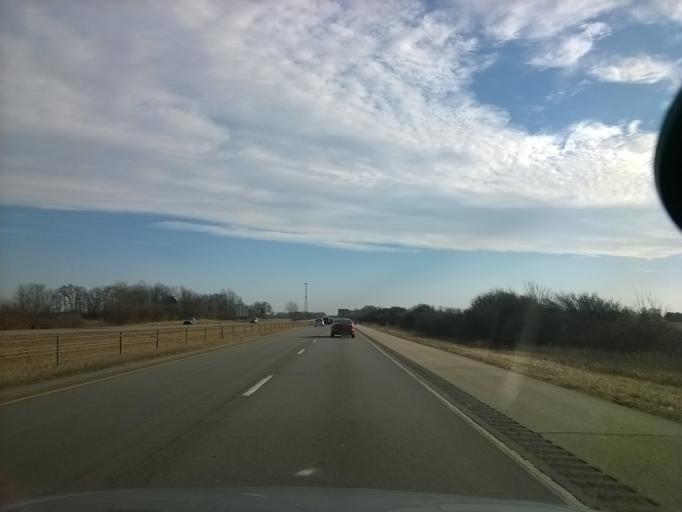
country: US
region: Indiana
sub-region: Johnson County
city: Franklin
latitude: 39.4661
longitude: -86.0060
